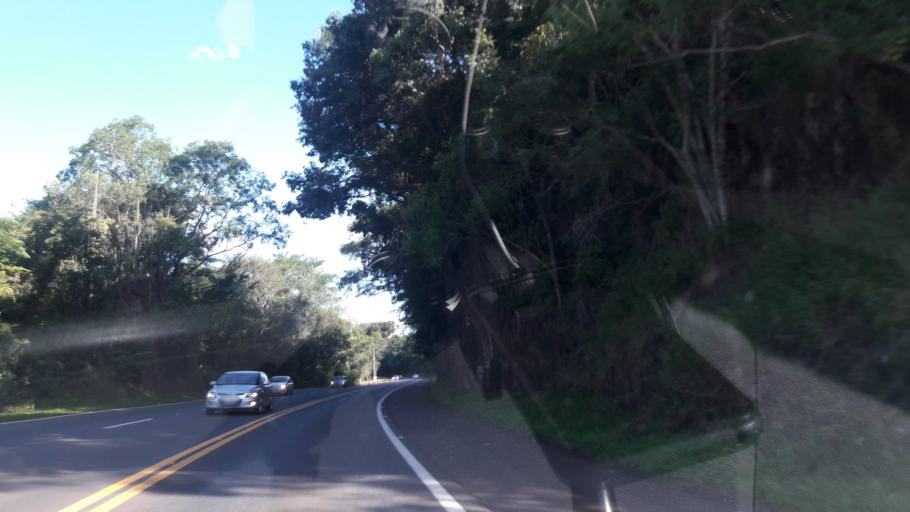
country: BR
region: Parana
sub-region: Laranjeiras Do Sul
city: Laranjeiras do Sul
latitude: -25.4062
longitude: -52.0909
